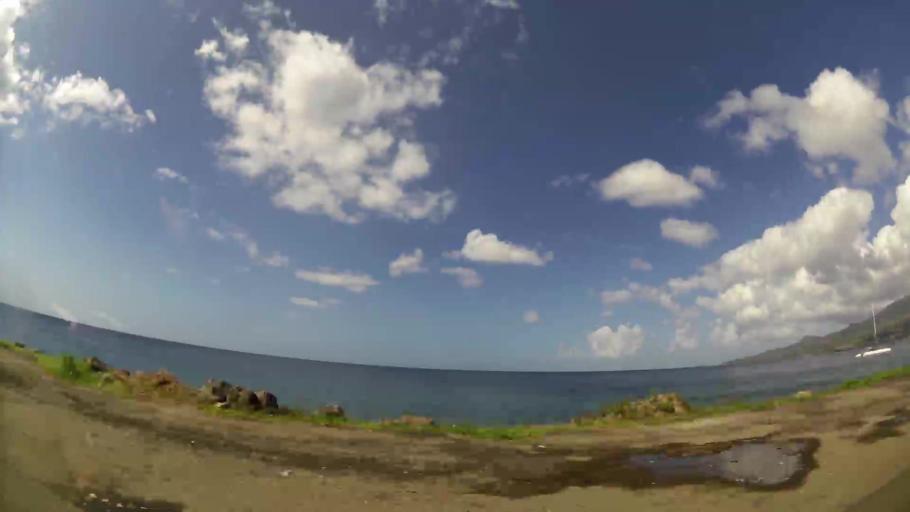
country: MQ
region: Martinique
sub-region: Martinique
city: Saint-Pierre
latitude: 14.7249
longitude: -61.1813
